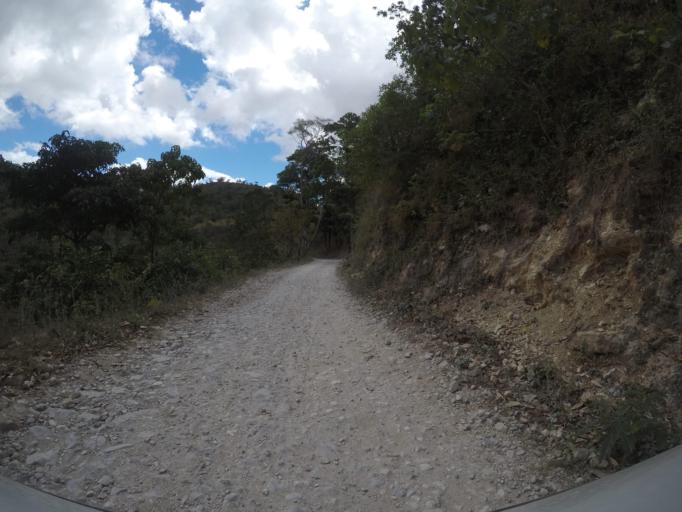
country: TL
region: Baucau
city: Baucau
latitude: -8.5252
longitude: 126.6917
